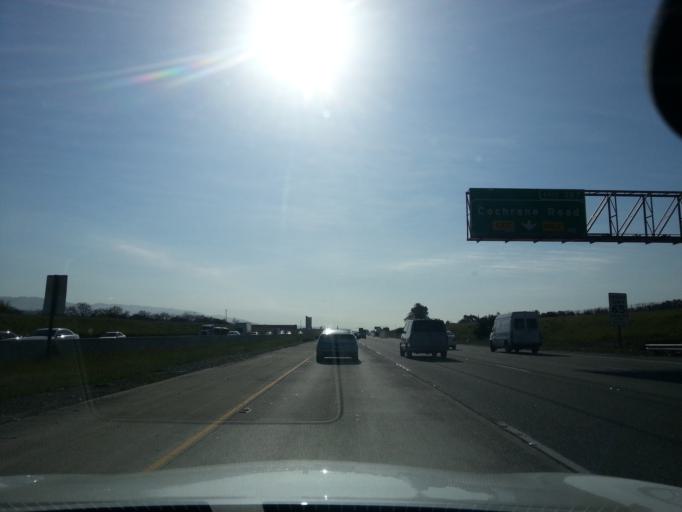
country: US
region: California
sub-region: Santa Clara County
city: Morgan Hill
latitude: 37.1613
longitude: -121.6617
